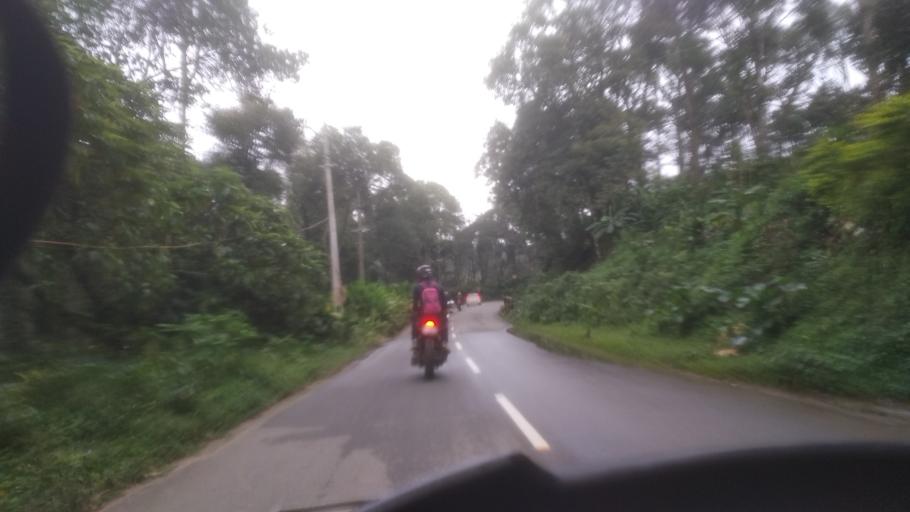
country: IN
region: Tamil Nadu
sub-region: Theni
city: Kombai
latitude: 9.8964
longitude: 77.1947
